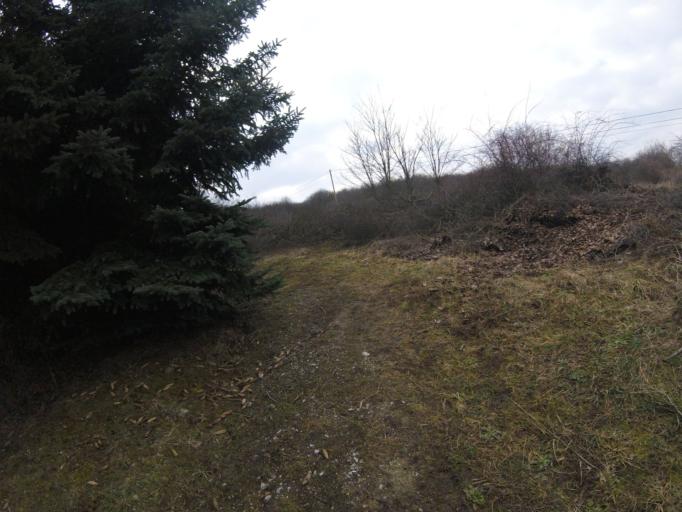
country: HU
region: Heves
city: Egerszalok
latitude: 47.8665
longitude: 20.3169
